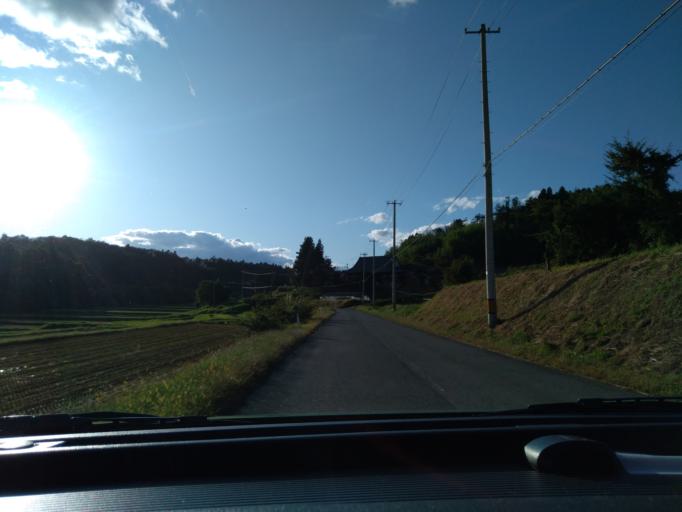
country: JP
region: Iwate
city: Ichinoseki
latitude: 38.8680
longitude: 141.1856
